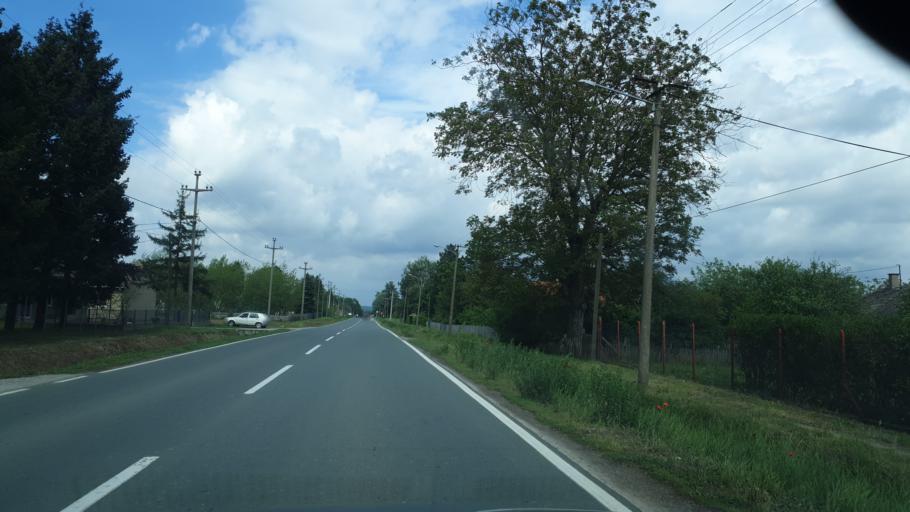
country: RS
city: Stubline
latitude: 44.5449
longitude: 20.1325
